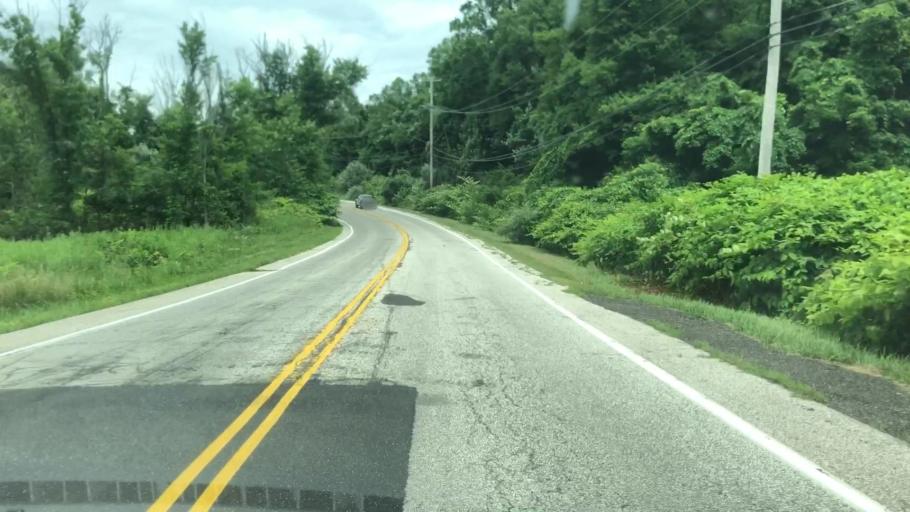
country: US
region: Ohio
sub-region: Summit County
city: Peninsula
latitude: 41.1775
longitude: -81.5594
